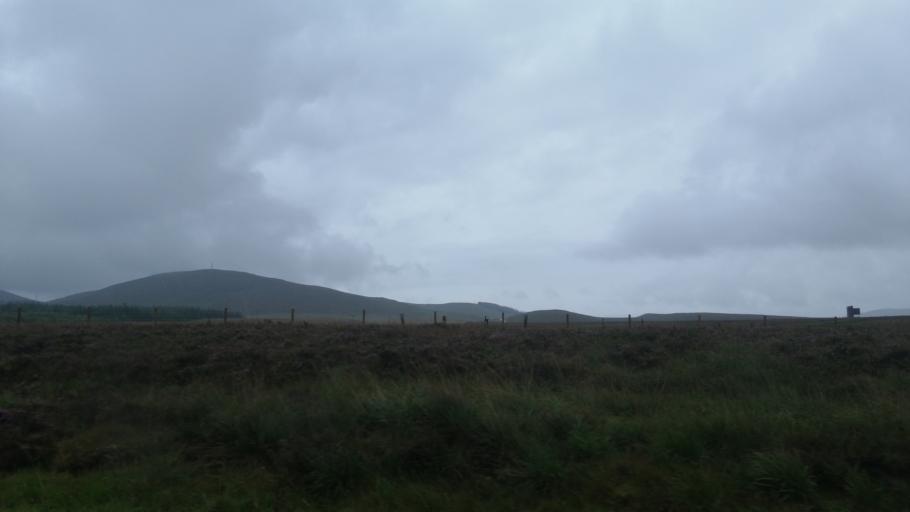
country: GB
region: Scotland
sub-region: Highland
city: Brora
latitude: 58.3565
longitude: -3.9006
